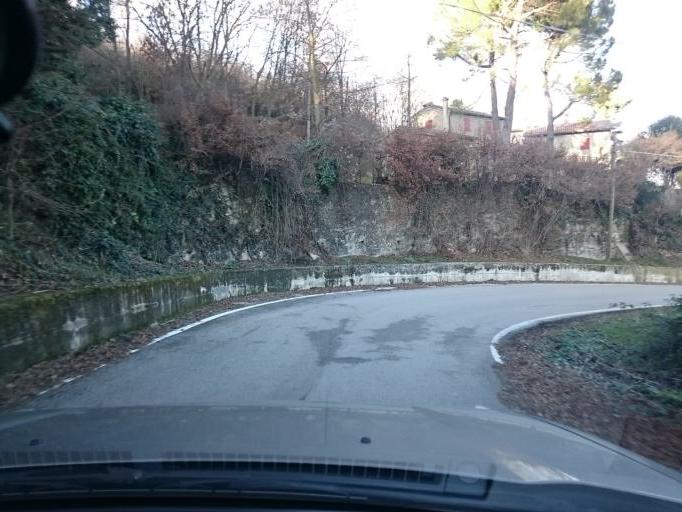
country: IT
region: Veneto
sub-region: Provincia di Padova
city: Treponti
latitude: 45.3588
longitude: 11.6809
